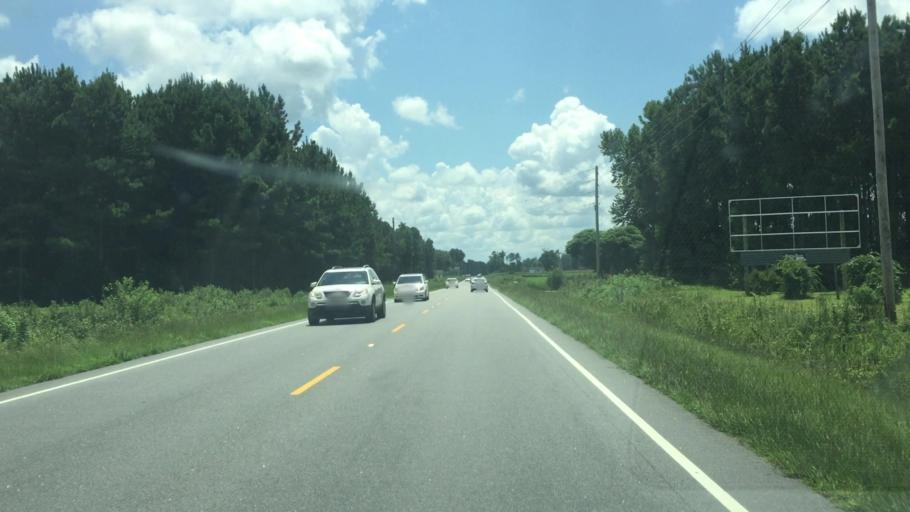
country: US
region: North Carolina
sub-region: Columbus County
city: Tabor City
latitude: 34.2261
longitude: -78.8243
